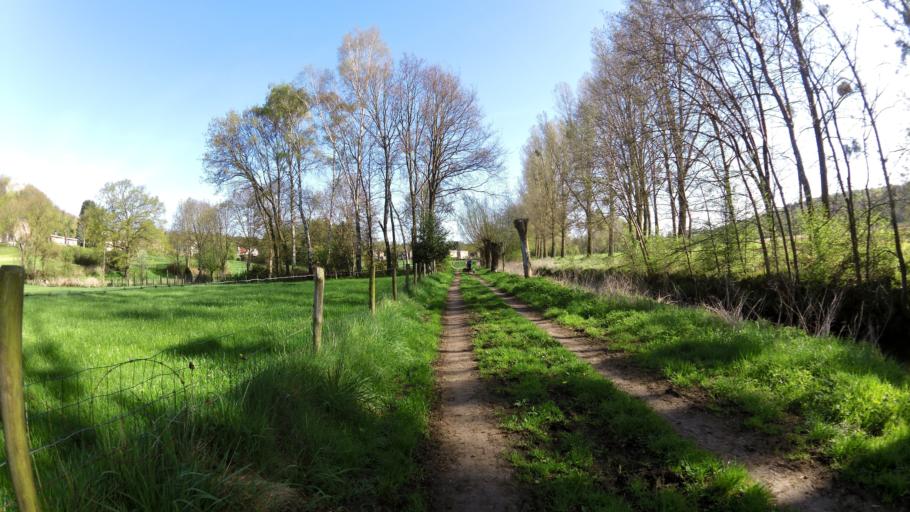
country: DE
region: North Rhine-Westphalia
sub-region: Regierungsbezirk Koln
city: Herzogenrath
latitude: 50.9079
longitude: 6.0805
